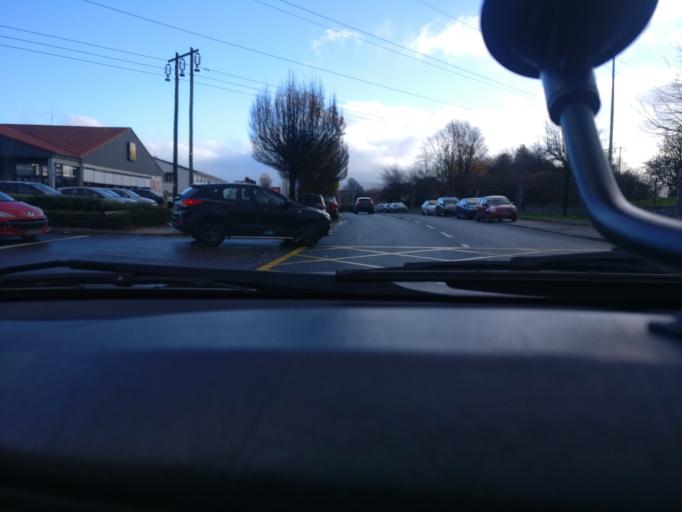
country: IE
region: Leinster
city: Crumlin
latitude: 53.3223
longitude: -6.3406
